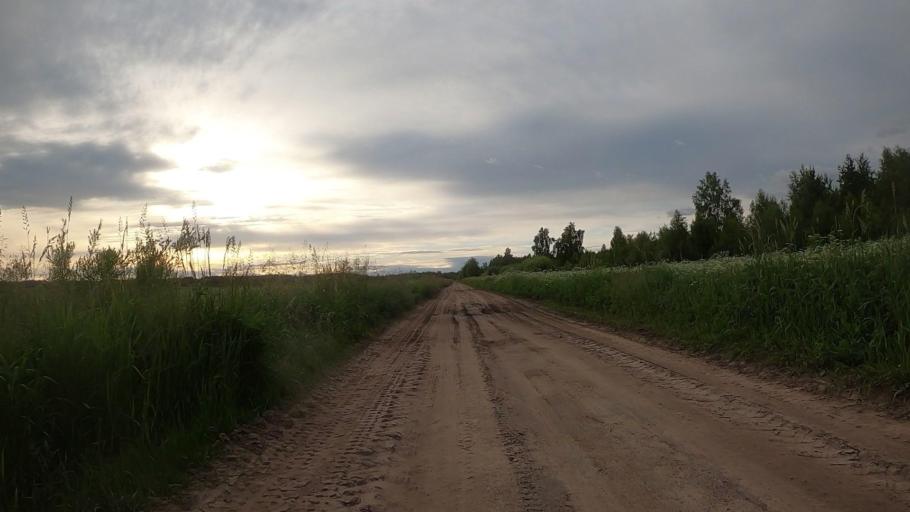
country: LV
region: Olaine
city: Olaine
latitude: 56.8252
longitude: 23.9677
